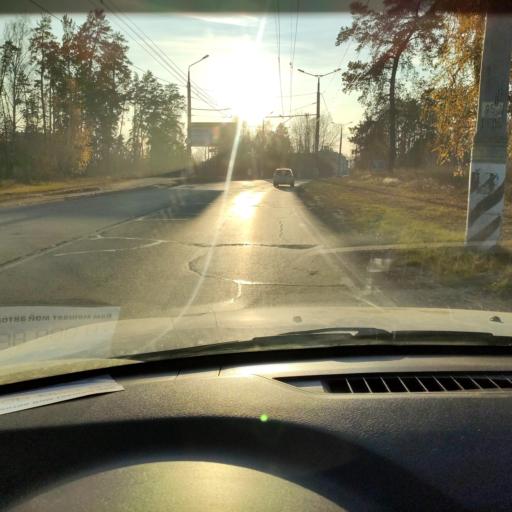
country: RU
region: Samara
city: Tol'yatti
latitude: 53.4790
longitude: 49.3721
